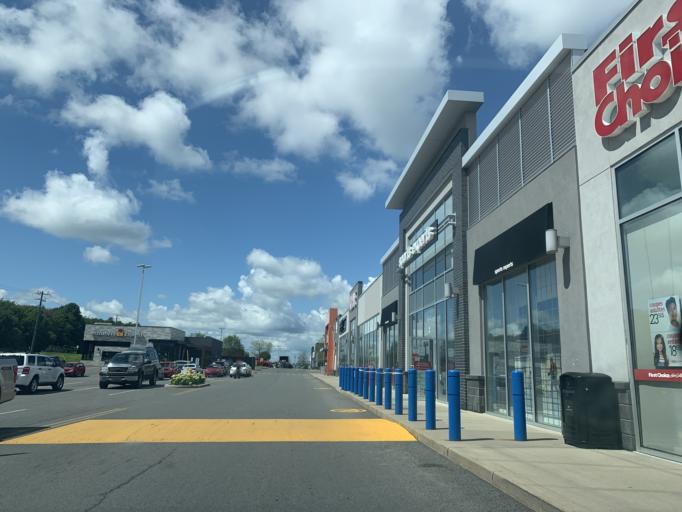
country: CA
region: Ontario
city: Hawkesbury
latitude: 45.5912
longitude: -74.5945
